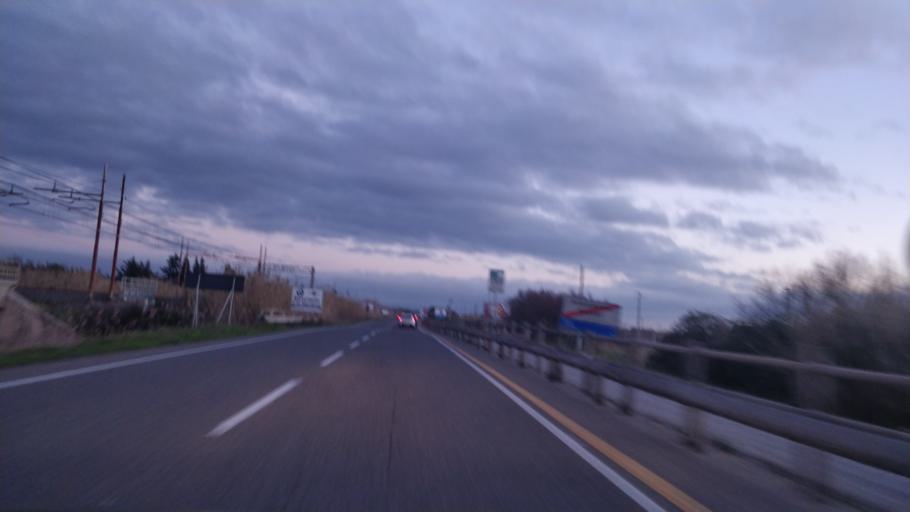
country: IT
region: Tuscany
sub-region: Provincia di Livorno
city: Rosignano Solvay-Castiglioncello
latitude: 43.3774
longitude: 10.4461
